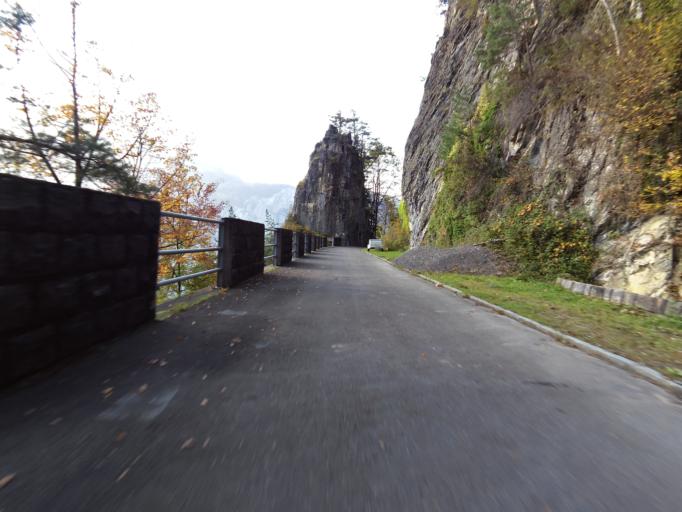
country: CH
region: Uri
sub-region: Uri
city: Bauen
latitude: 46.9394
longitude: 8.6171
